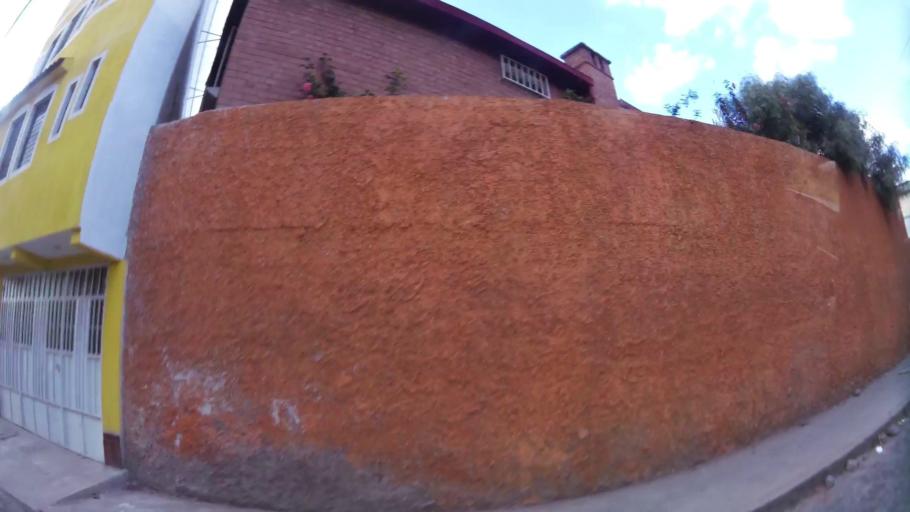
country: GT
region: Quetzaltenango
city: Quetzaltenango
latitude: 14.8406
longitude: -91.5293
